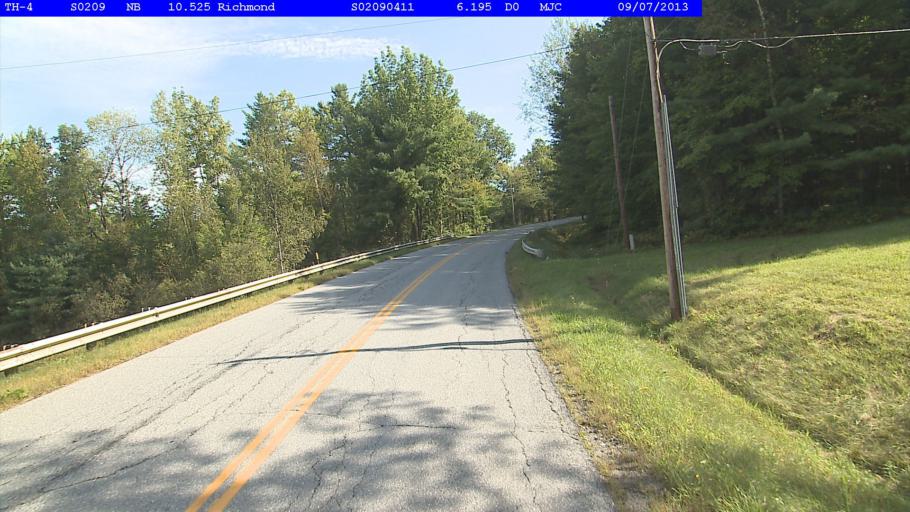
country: US
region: Vermont
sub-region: Chittenden County
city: Williston
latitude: 44.4178
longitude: -72.9862
